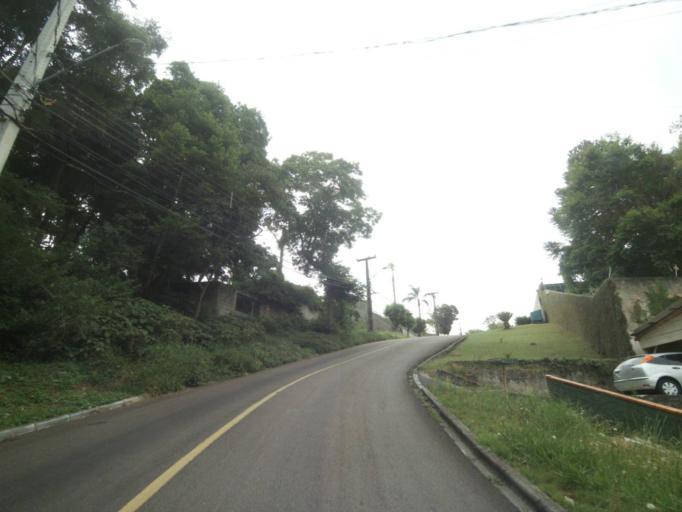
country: BR
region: Parana
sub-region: Curitiba
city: Curitiba
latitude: -25.4097
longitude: -49.3098
